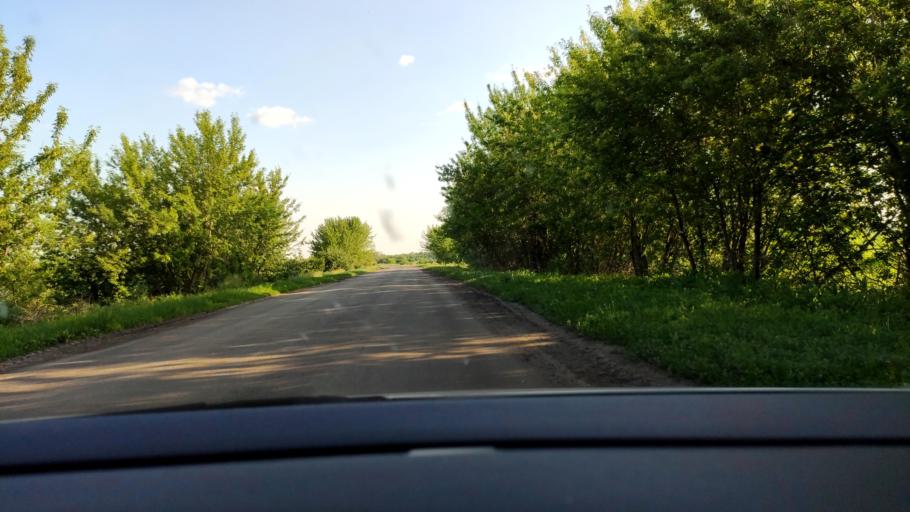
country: RU
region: Voronezj
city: Kashirskoye
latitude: 51.5212
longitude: 39.8347
